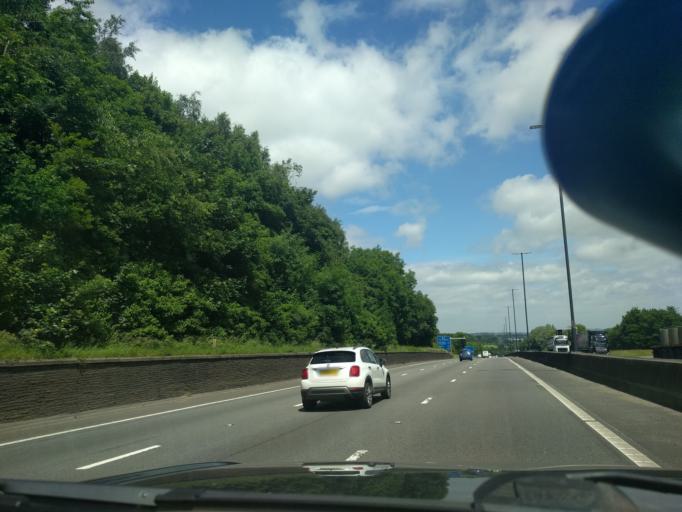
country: GB
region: Wales
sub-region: Newport
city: Newport
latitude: 51.5854
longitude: -3.0347
